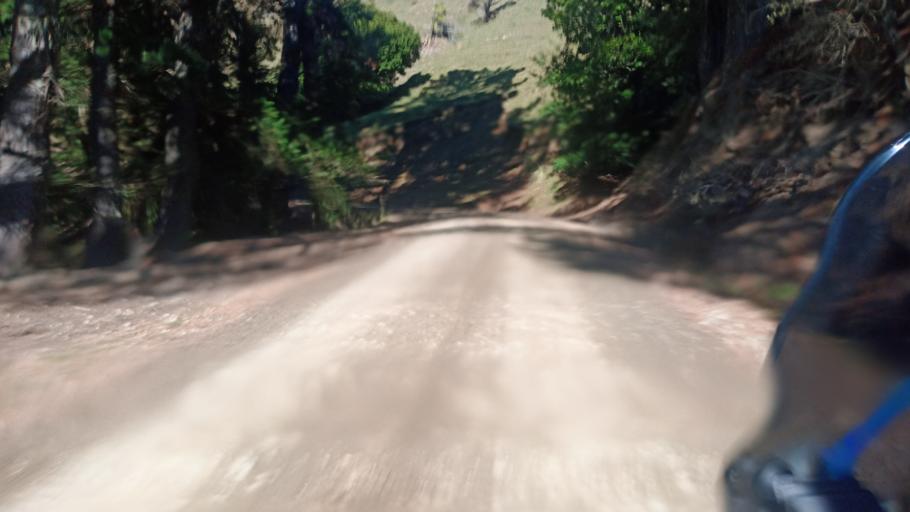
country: NZ
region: Gisborne
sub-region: Gisborne District
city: Gisborne
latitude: -38.2872
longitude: 177.8598
